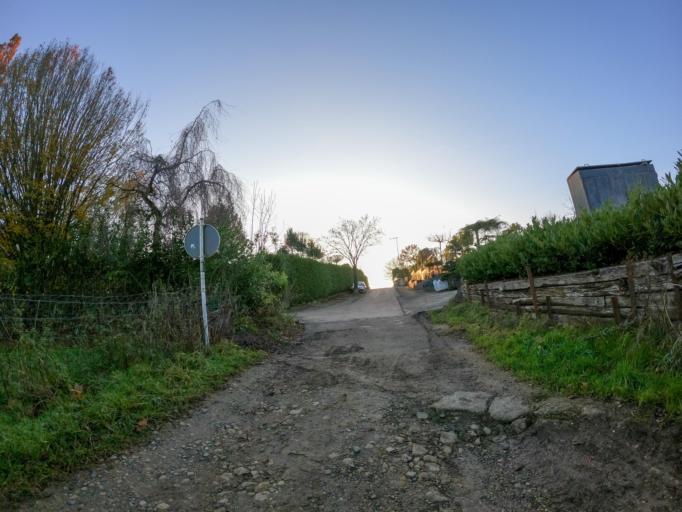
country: LU
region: Luxembourg
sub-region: Canton de Capellen
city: Dippach
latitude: 49.5943
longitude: 5.9907
